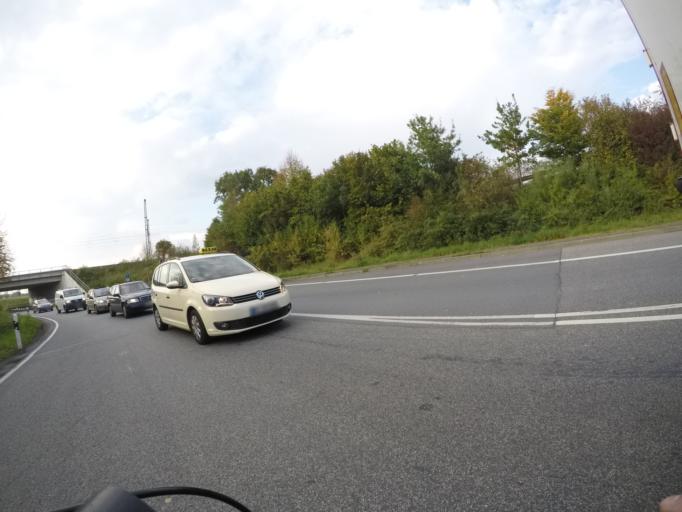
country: DE
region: North Rhine-Westphalia
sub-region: Regierungsbezirk Detmold
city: Herford
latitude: 52.1041
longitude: 8.6446
